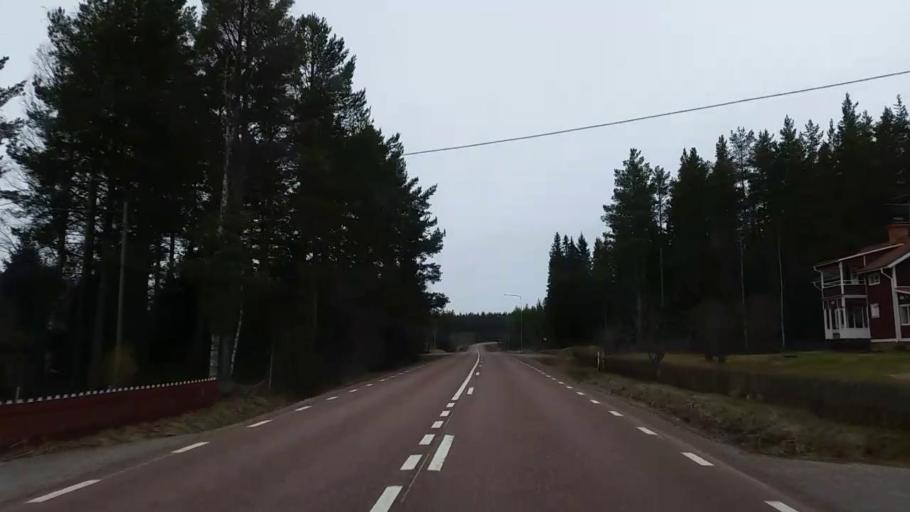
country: SE
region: Gaevleborg
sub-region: Ovanakers Kommun
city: Edsbyn
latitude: 61.2064
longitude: 15.8713
